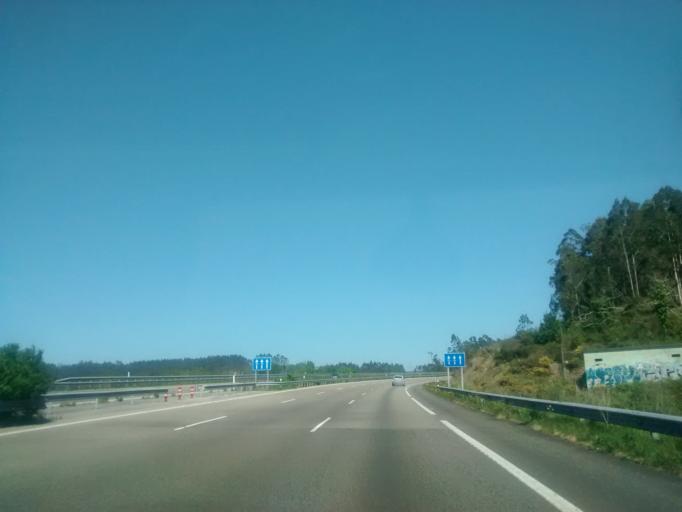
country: ES
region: Asturias
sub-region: Province of Asturias
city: Villaviciosa
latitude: 43.5026
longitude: -5.3569
